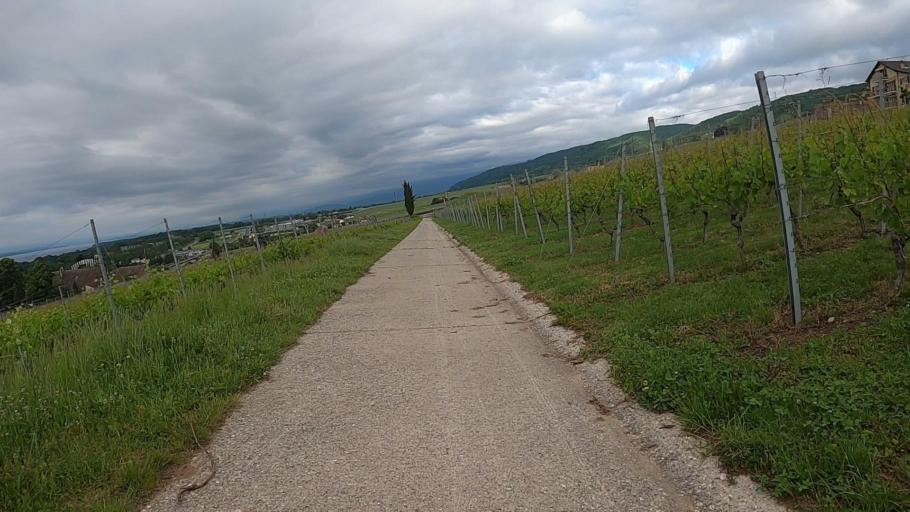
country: CH
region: Vaud
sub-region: Nyon District
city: Rolle
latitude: 46.4698
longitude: 6.3358
